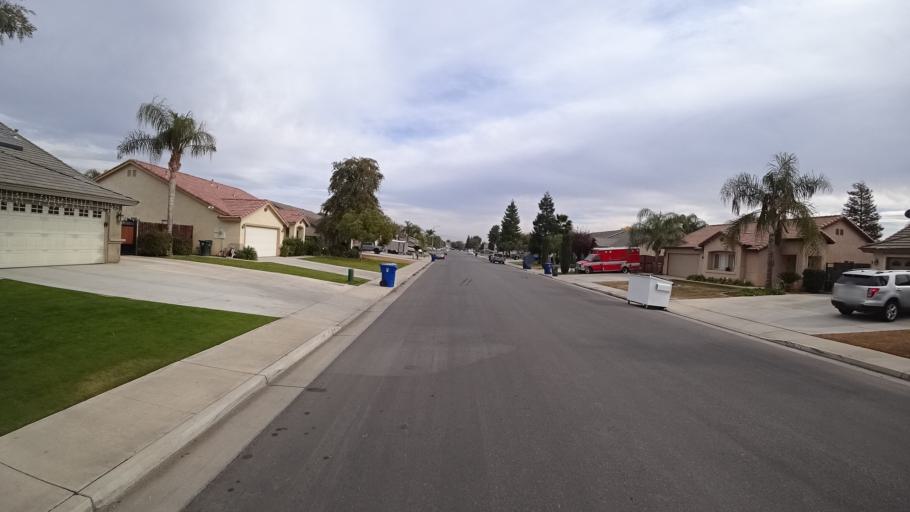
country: US
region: California
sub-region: Kern County
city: Rosedale
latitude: 35.4221
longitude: -119.1363
